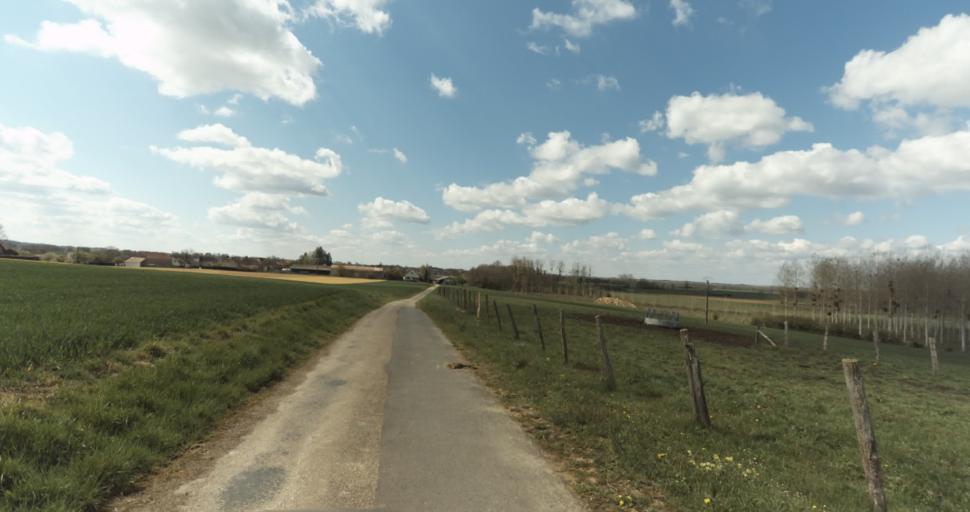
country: FR
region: Bourgogne
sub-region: Departement de la Cote-d'Or
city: Auxonne
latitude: 47.2131
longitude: 5.4151
